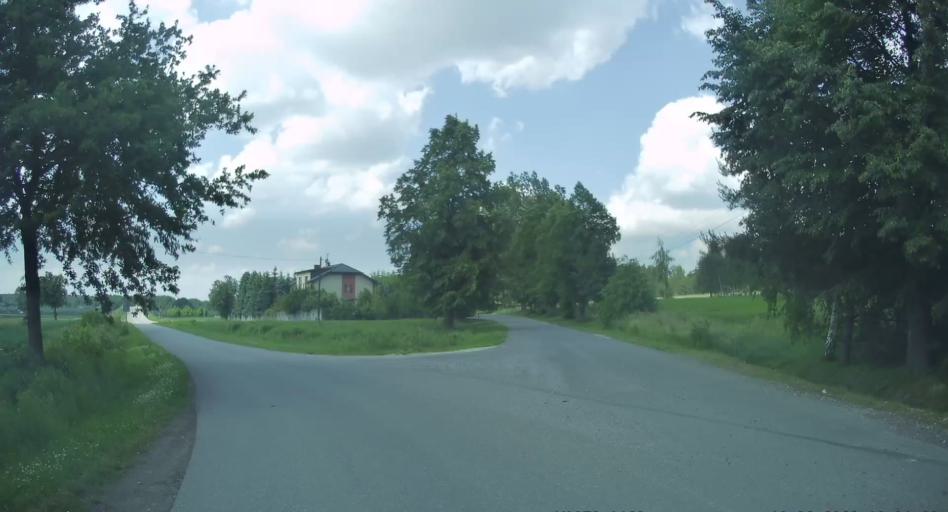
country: PL
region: Lodz Voivodeship
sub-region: Powiat tomaszowski
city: Czerniewice
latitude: 51.6917
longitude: 20.2167
